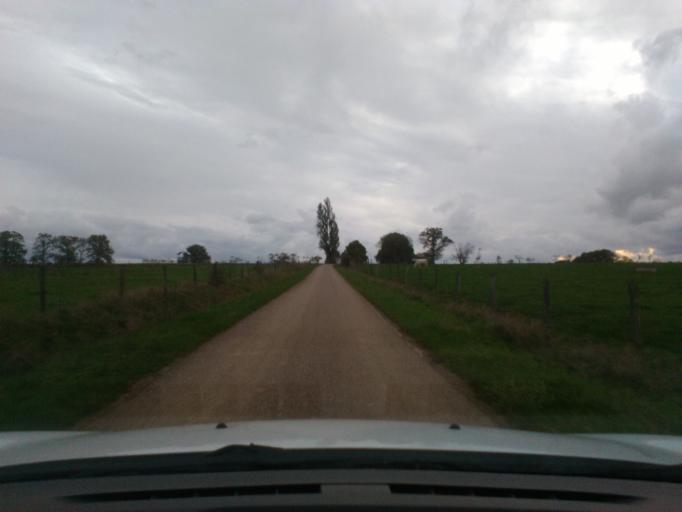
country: FR
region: Lorraine
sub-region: Departement des Vosges
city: Mirecourt
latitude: 48.3393
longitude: 6.0624
